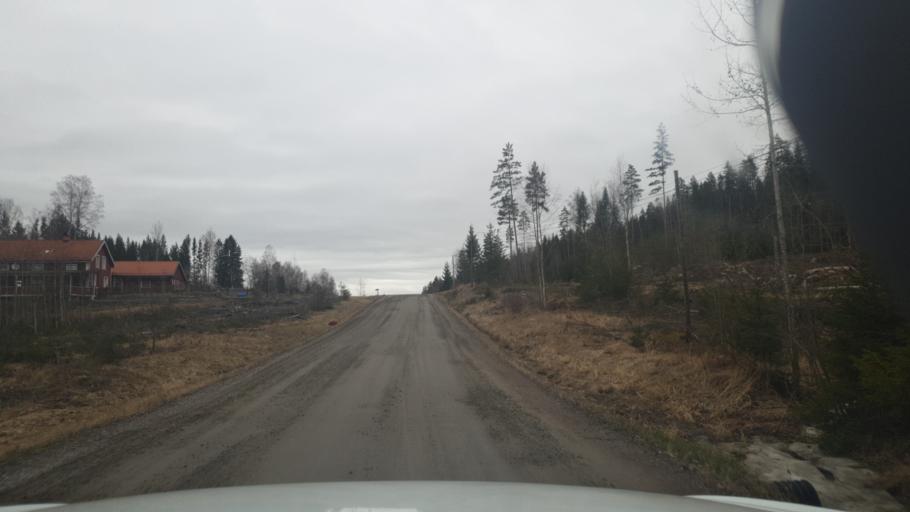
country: NO
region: Ostfold
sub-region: Romskog
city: Romskog
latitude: 59.8419
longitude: 11.9816
